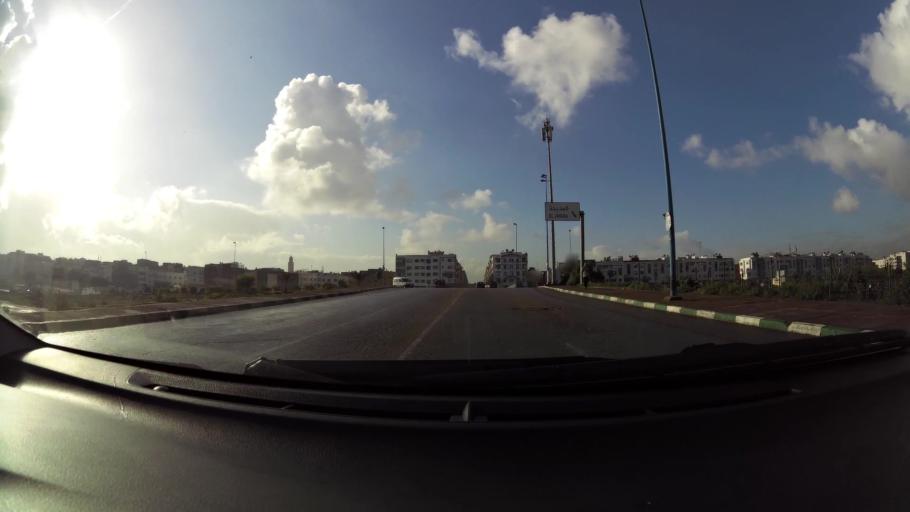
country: MA
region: Grand Casablanca
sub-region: Mediouna
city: Tit Mellil
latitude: 33.5964
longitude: -7.5194
